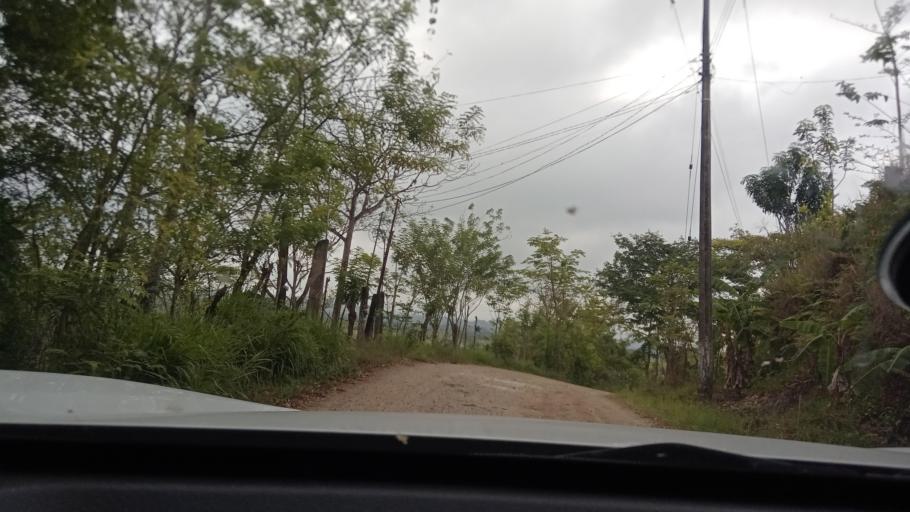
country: MX
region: Tabasco
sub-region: Huimanguillo
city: Francisco Rueda
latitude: 17.5671
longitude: -94.0280
